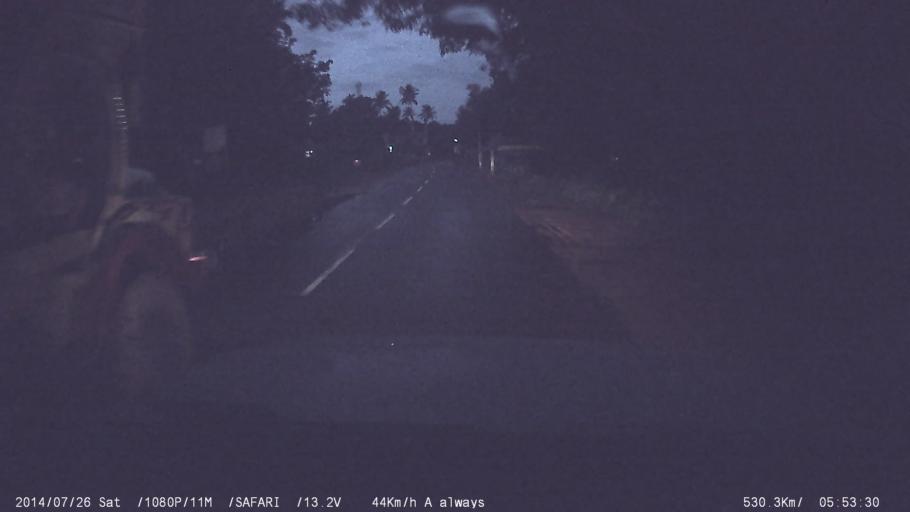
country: IN
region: Kerala
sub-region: Ernakulam
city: Muvattupuzha
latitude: 9.9541
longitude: 76.5753
